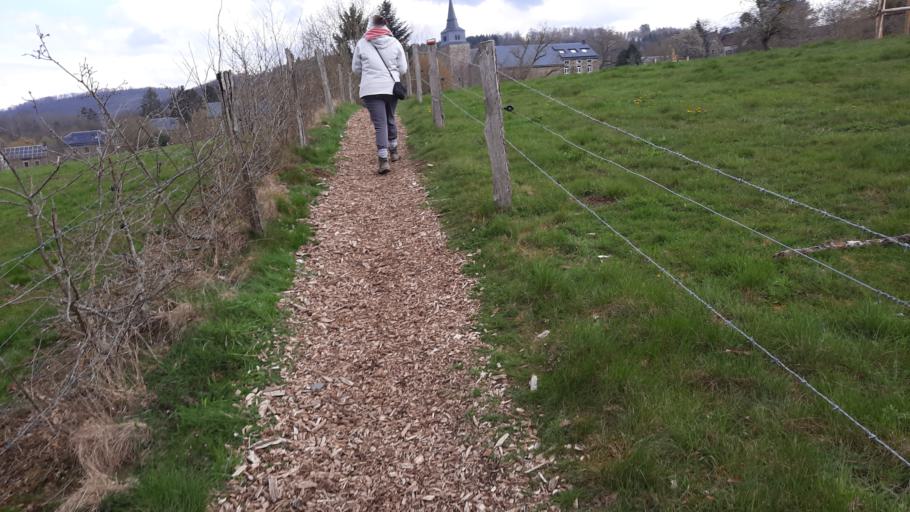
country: BE
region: Wallonia
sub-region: Province du Luxembourg
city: Rendeux
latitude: 50.2132
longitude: 5.5264
